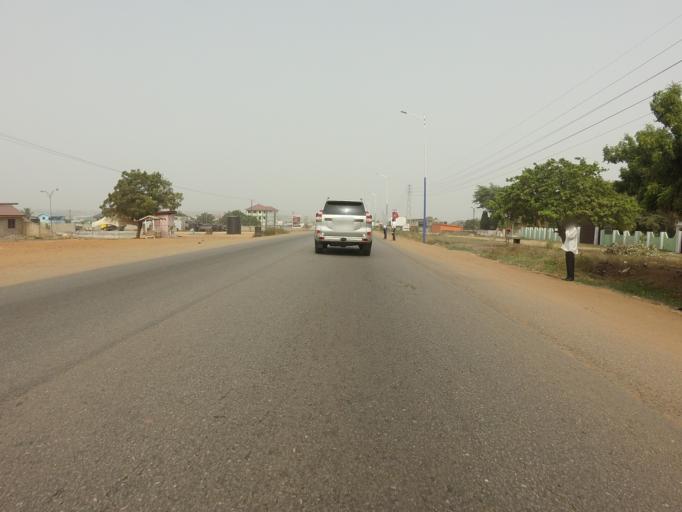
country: GH
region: Greater Accra
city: Tema
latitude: 5.7543
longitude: 0.0462
